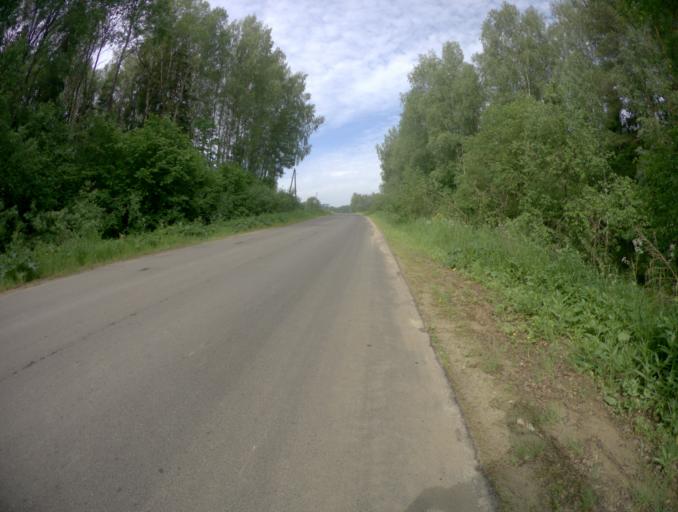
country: RU
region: Vladimir
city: Lakinsk
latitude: 56.0670
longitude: 39.9257
